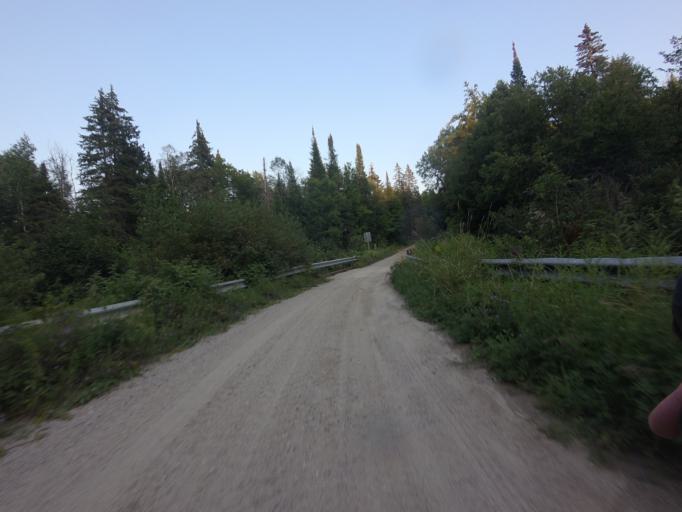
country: CA
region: Ontario
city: Renfrew
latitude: 45.0777
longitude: -76.7230
